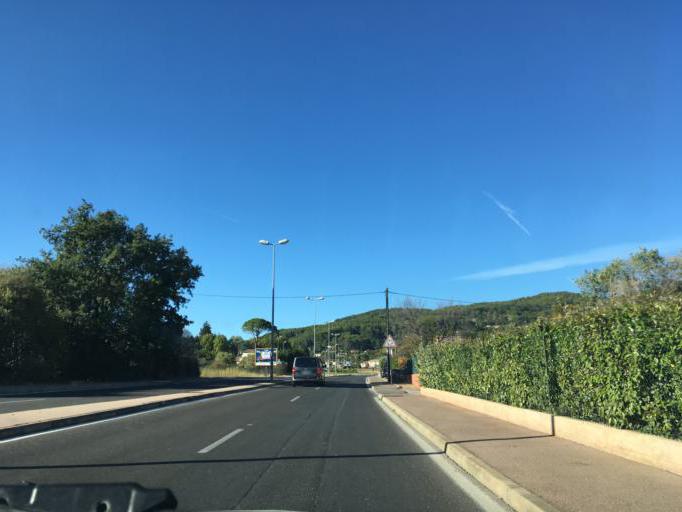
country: FR
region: Provence-Alpes-Cote d'Azur
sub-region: Departement du Var
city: Draguignan
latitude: 43.5426
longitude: 6.4459
